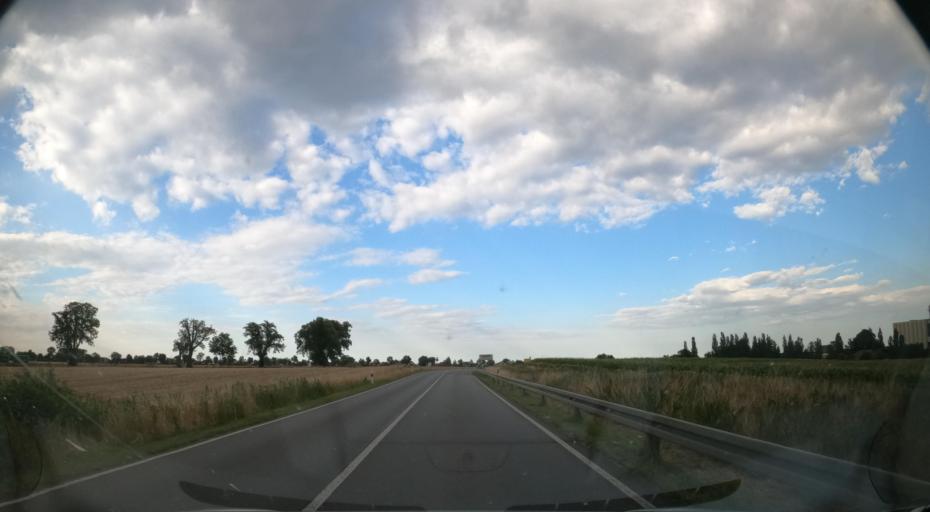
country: DE
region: Mecklenburg-Vorpommern
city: Pasewalk
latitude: 53.5136
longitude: 13.9725
